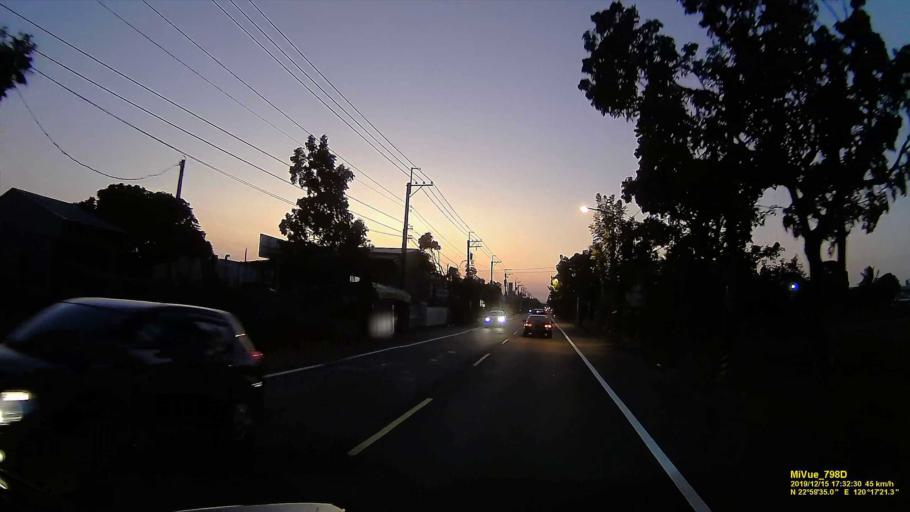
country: TW
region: Taiwan
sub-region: Tainan
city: Tainan
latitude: 22.9930
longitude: 120.2889
